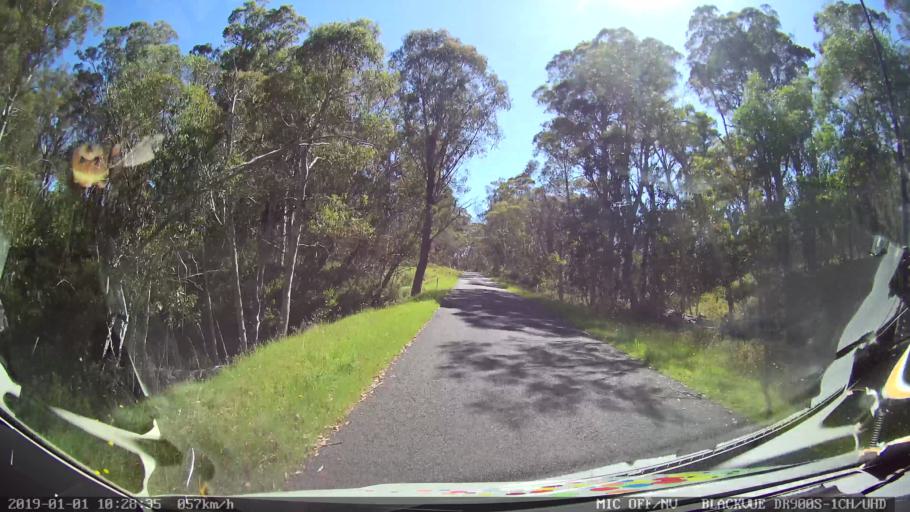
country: AU
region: New South Wales
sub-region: Snowy River
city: Jindabyne
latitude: -36.0594
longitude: 148.2417
